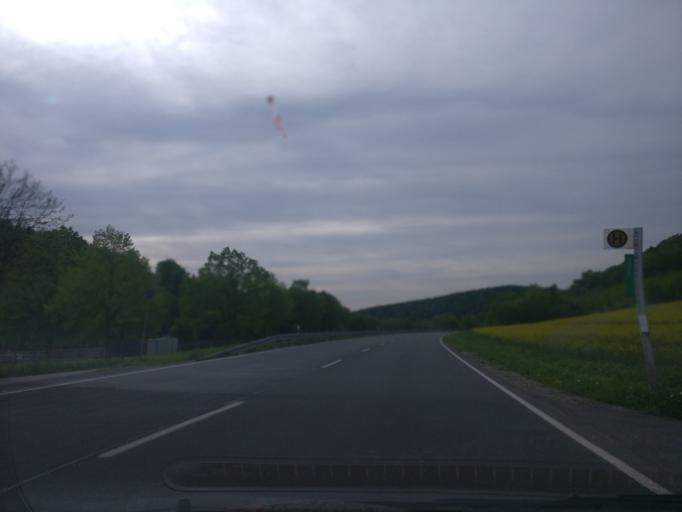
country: DE
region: Hesse
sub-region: Regierungsbezirk Kassel
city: Fuldatal
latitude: 51.3638
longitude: 9.5478
